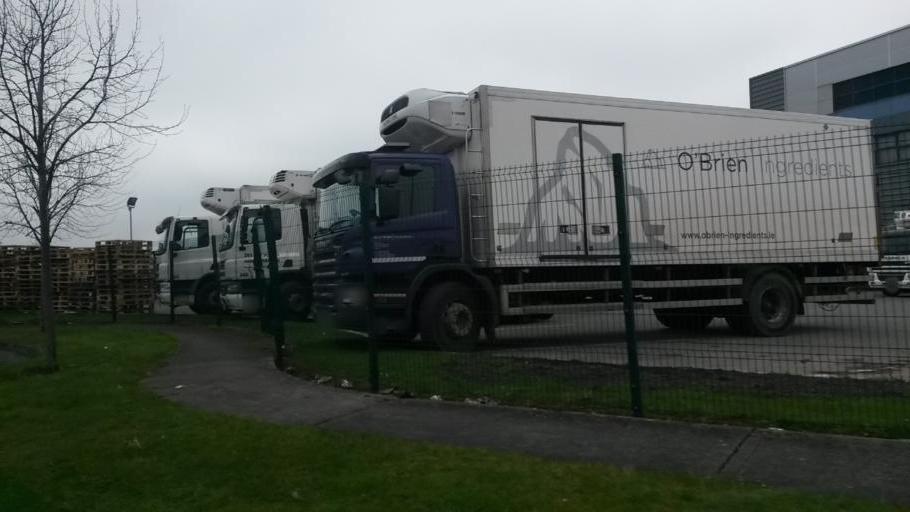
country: IE
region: Leinster
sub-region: Dublin City
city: Finglas
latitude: 53.3977
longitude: -6.3206
